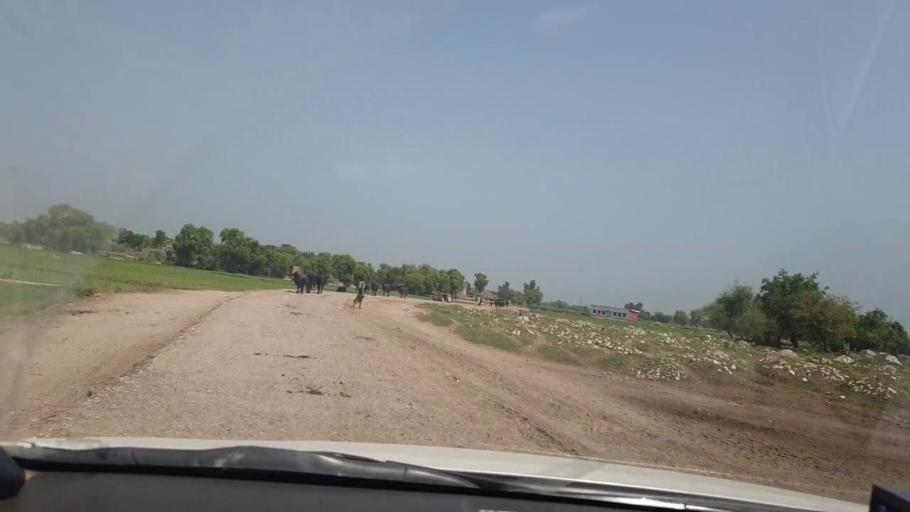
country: PK
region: Sindh
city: Chak
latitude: 27.8786
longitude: 68.7823
